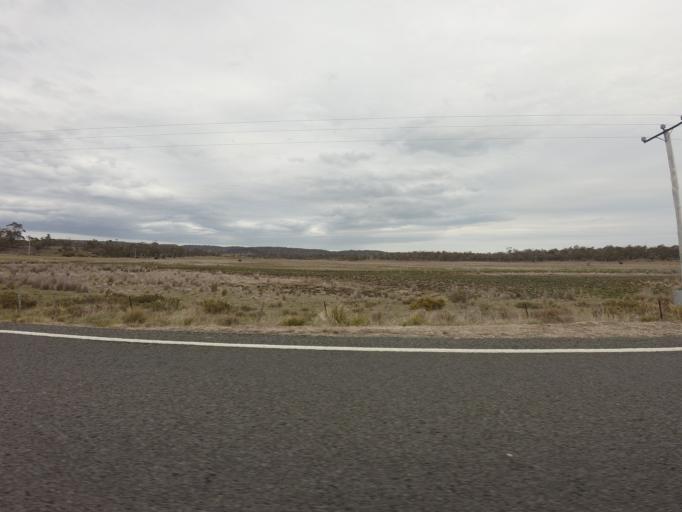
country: AU
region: Tasmania
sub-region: Break O'Day
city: St Helens
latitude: -42.0435
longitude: 148.0526
